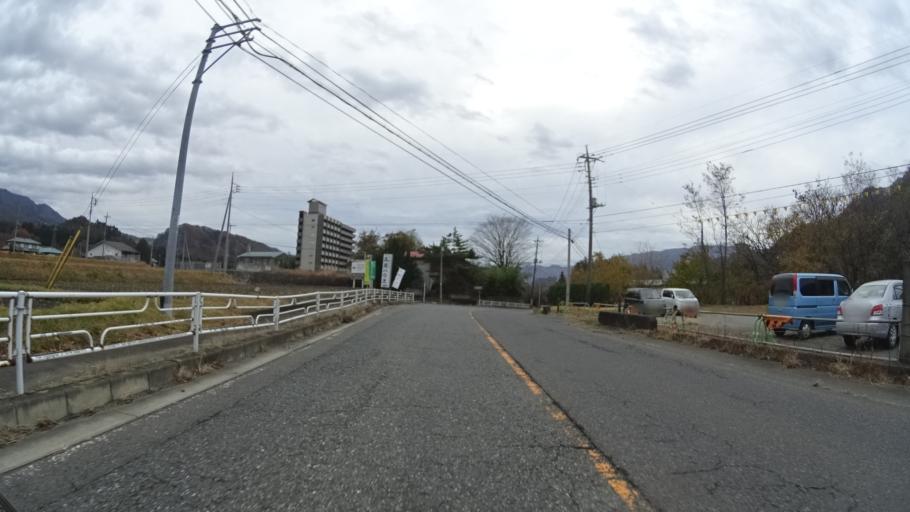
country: JP
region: Gunma
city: Nakanojomachi
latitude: 36.7166
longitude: 138.8952
